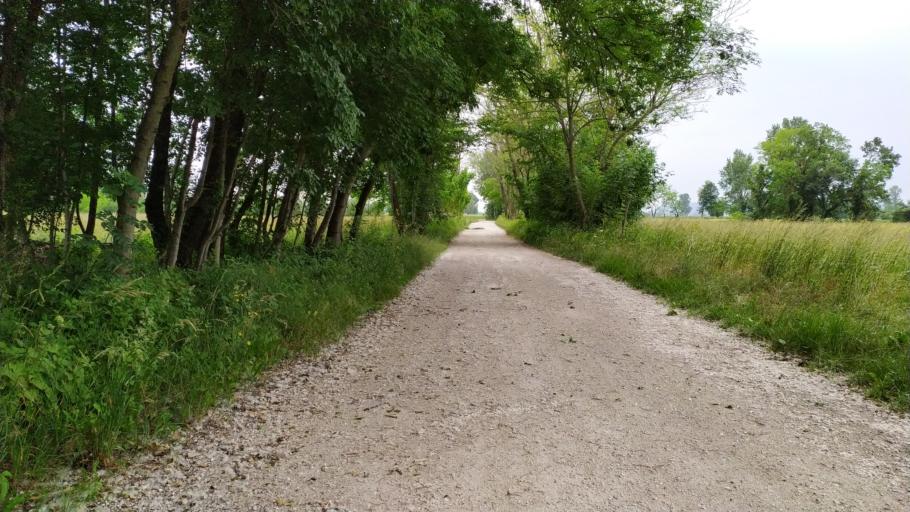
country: IT
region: Friuli Venezia Giulia
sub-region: Provincia di Udine
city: Osoppo
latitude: 46.2429
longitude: 13.0687
